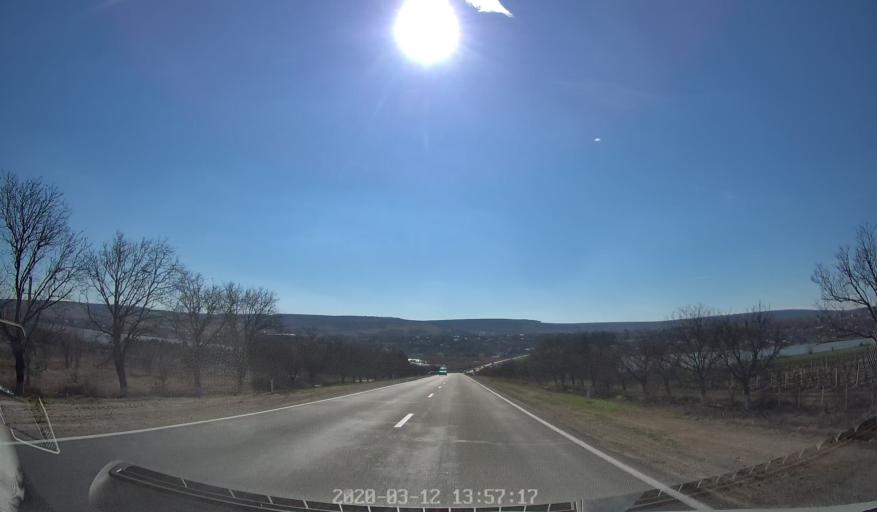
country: MD
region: Chisinau
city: Vatra
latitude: 46.9927
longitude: 28.6915
